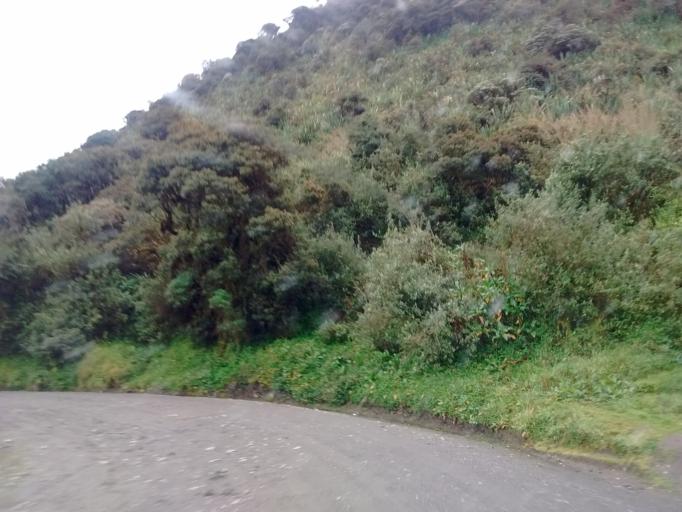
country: CO
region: Cauca
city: Totoro
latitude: 2.3516
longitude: -76.3133
